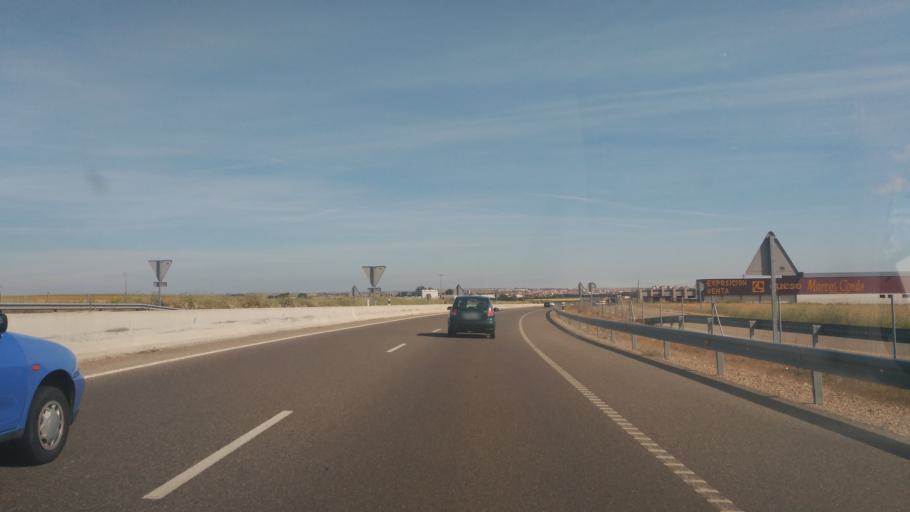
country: ES
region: Castille and Leon
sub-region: Provincia de Zamora
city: Morales del Vino
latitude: 41.4597
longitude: -5.7324
